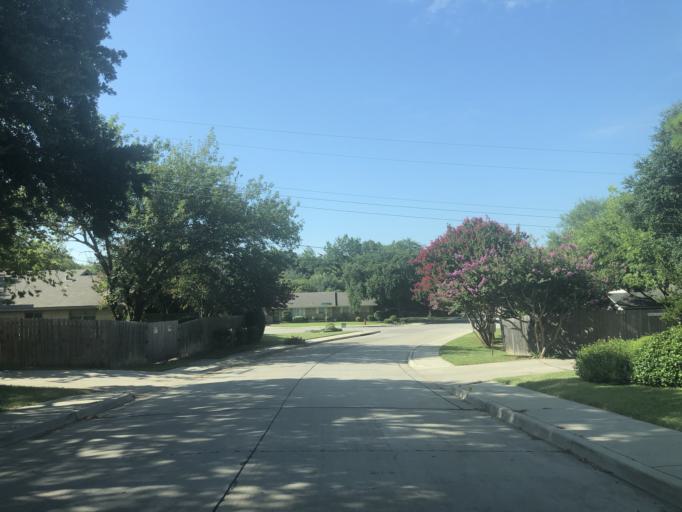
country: US
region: Texas
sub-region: Dallas County
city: Grand Prairie
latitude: 32.7547
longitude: -97.0216
